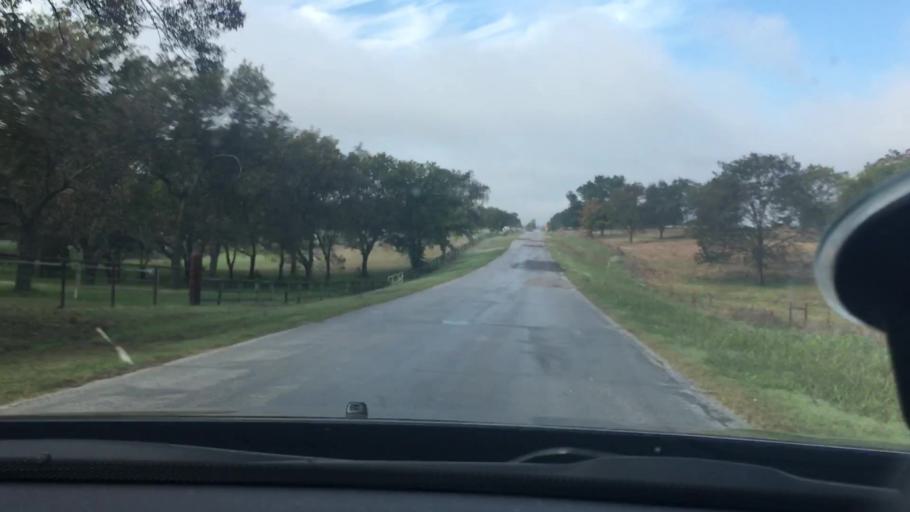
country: US
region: Oklahoma
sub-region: Murray County
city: Sulphur
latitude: 34.6223
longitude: -96.9611
